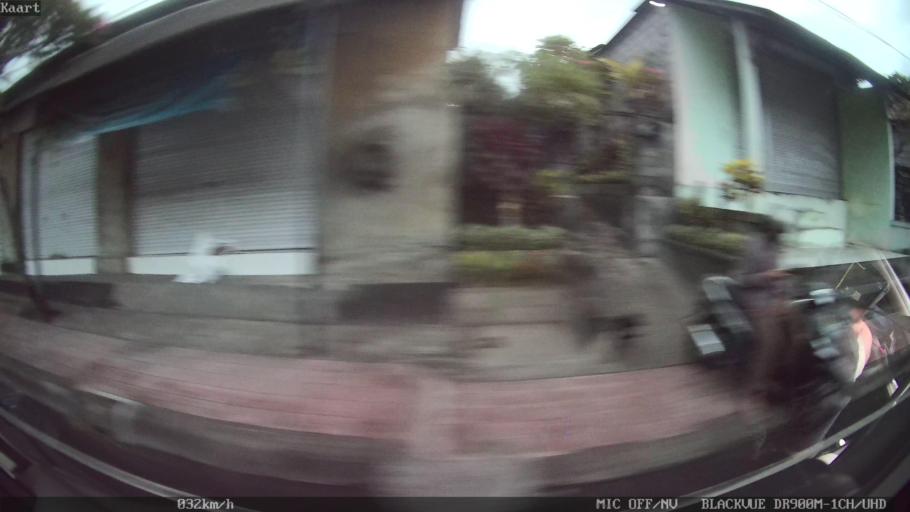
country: ID
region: Bali
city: Banjar Pasekan
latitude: -8.6219
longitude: 115.2842
